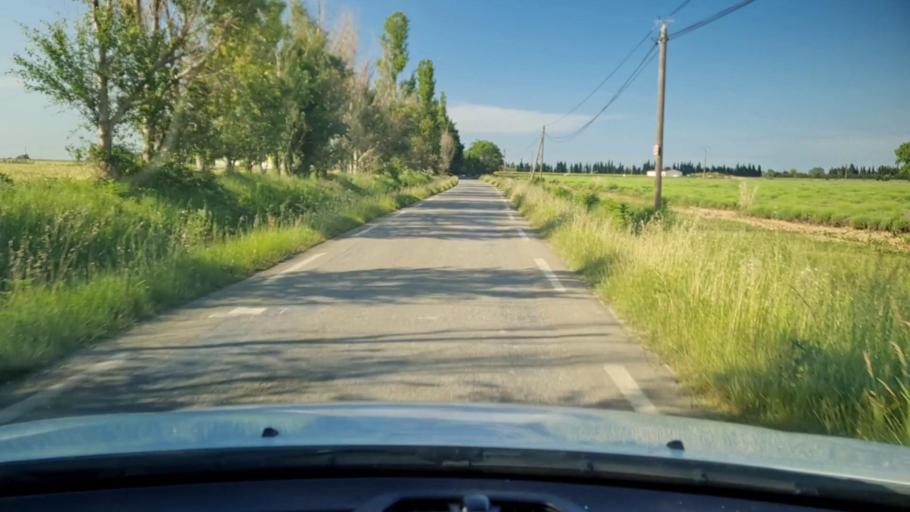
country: FR
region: Languedoc-Roussillon
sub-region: Departement du Gard
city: Aimargues
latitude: 43.6624
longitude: 4.2153
